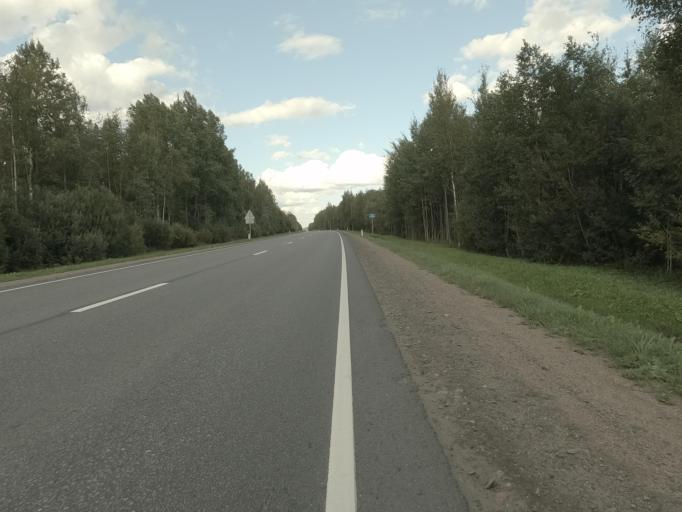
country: RU
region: Leningrad
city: Mga
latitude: 59.6807
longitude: 30.9491
